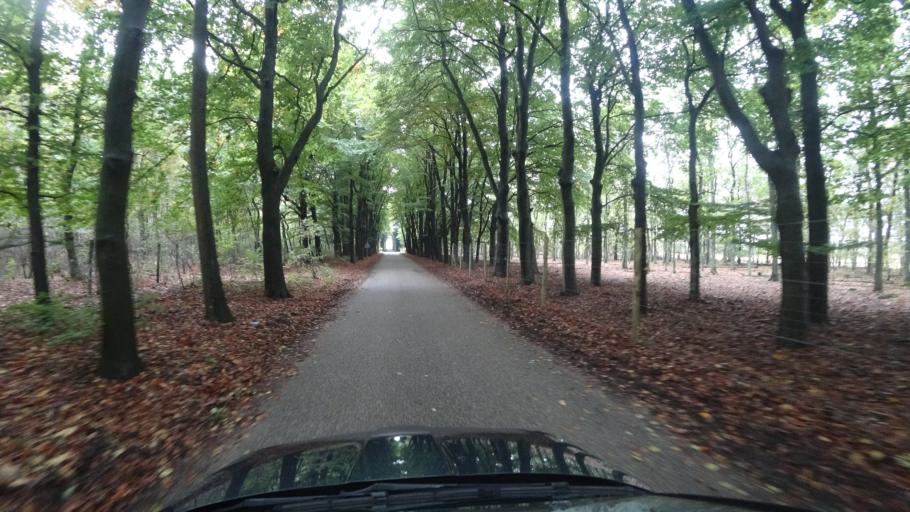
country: NL
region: Gelderland
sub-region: Gemeente Renkum
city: Heelsum
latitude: 52.0416
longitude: 5.7305
